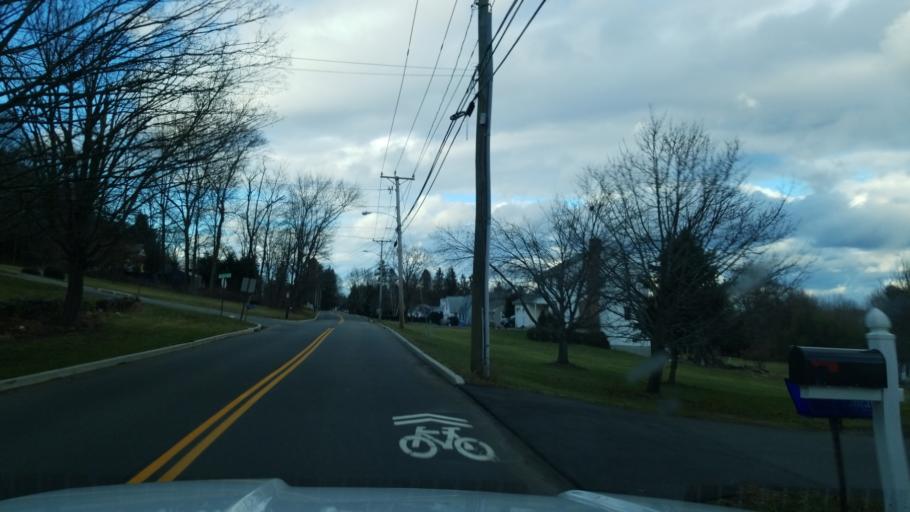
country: US
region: Connecticut
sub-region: Middlesex County
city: Middletown
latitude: 41.5211
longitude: -72.6335
